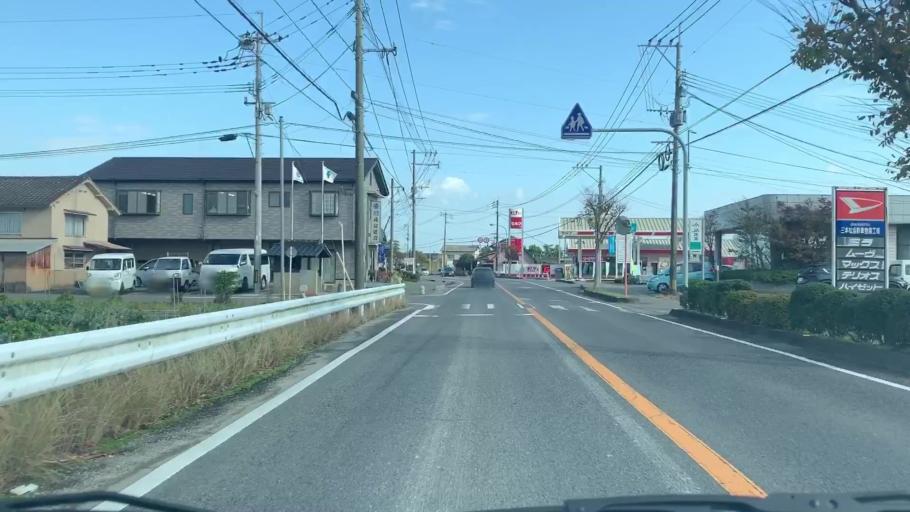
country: JP
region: Saga Prefecture
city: Kashima
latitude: 33.1247
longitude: 130.0713
